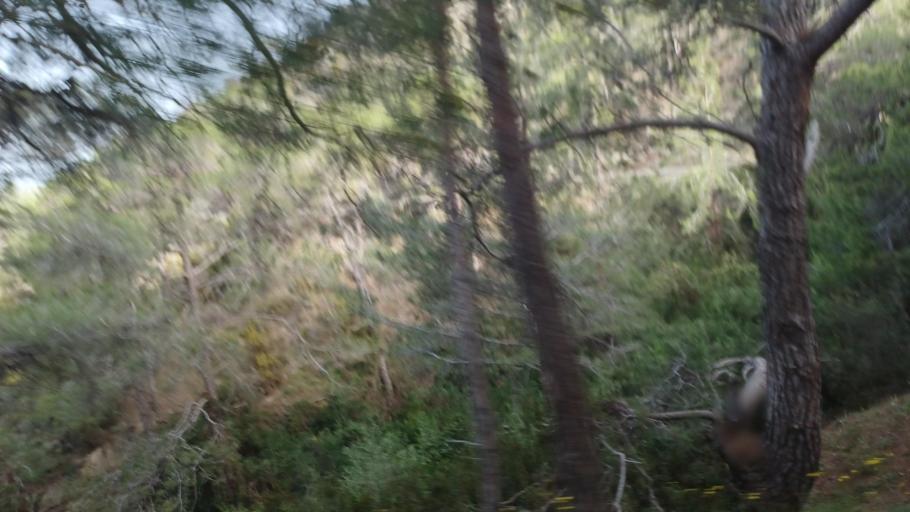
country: CY
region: Pafos
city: Polis
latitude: 35.0055
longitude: 32.3352
